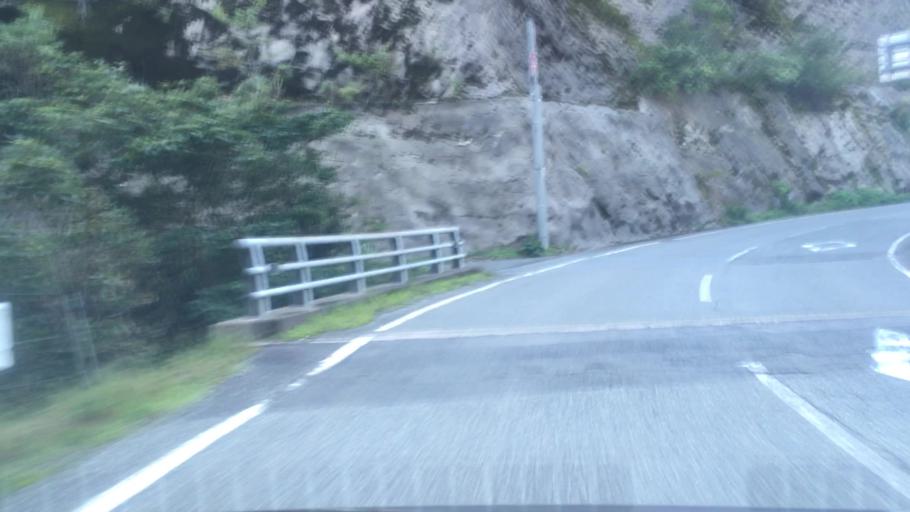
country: JP
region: Hyogo
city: Toyooka
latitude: 35.6055
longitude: 134.8078
